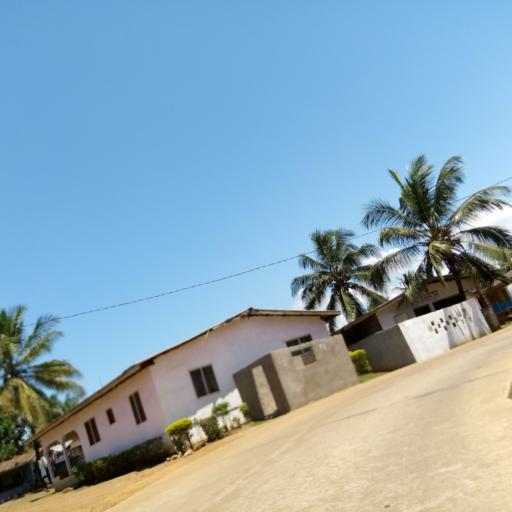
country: LR
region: Montserrado
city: Monrovia
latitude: 6.2466
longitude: -10.6919
